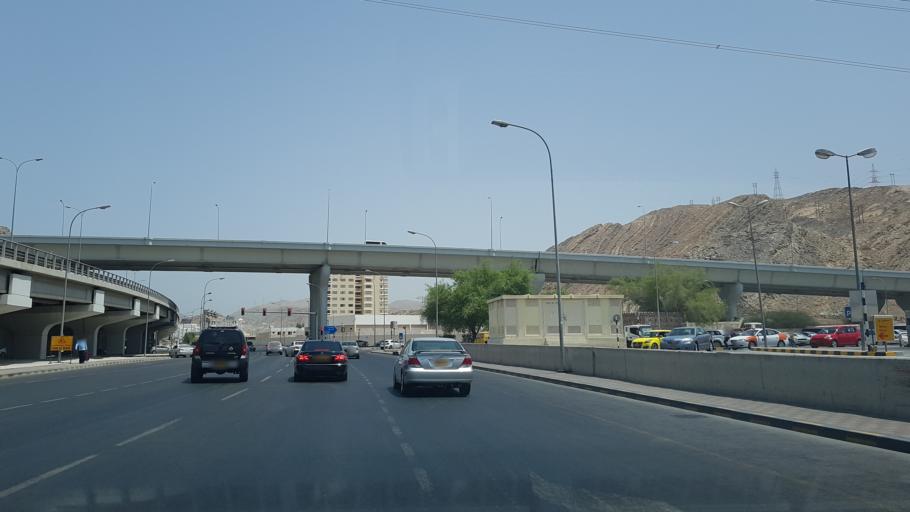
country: OM
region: Muhafazat Masqat
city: Muscat
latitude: 23.5917
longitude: 58.5253
